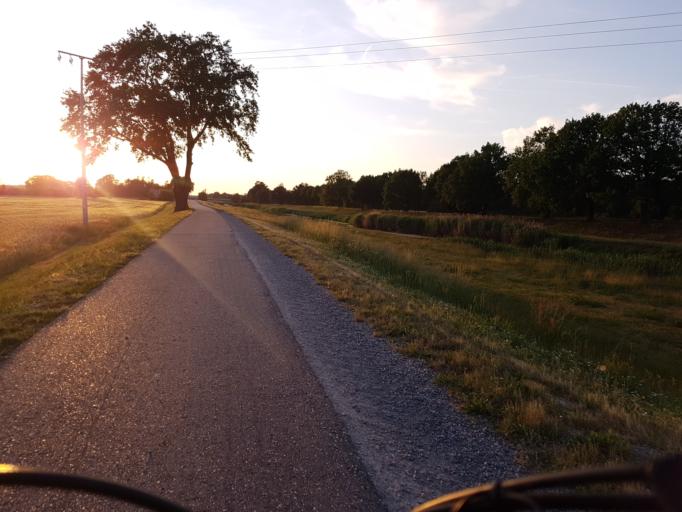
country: DE
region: Brandenburg
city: Schilda
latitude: 51.6008
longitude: 13.3201
